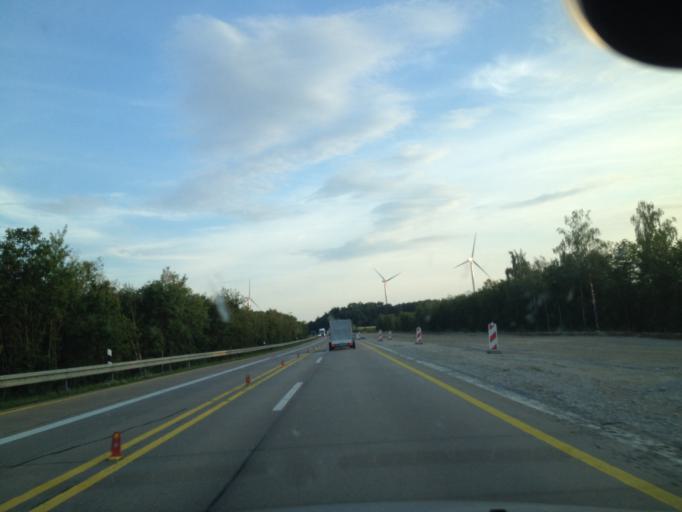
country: DE
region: Bavaria
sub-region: Regierungsbezirk Mittelfranken
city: Gollhofen
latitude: 49.5628
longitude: 10.1684
